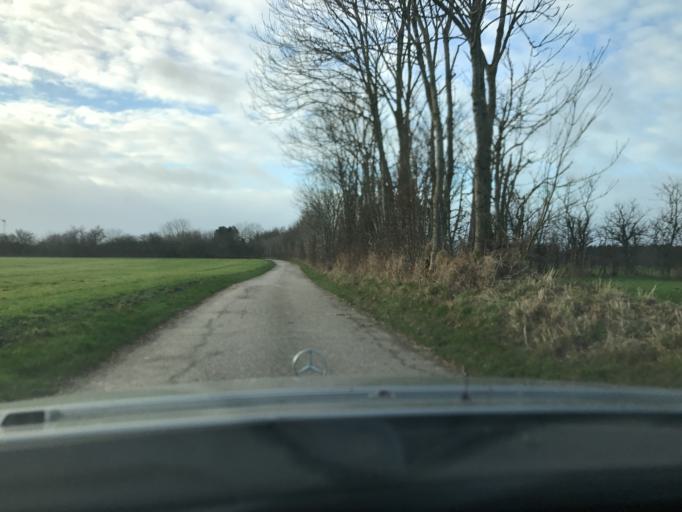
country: DK
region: South Denmark
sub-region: Sonderborg Kommune
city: Nordborg
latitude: 55.0514
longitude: 9.6653
